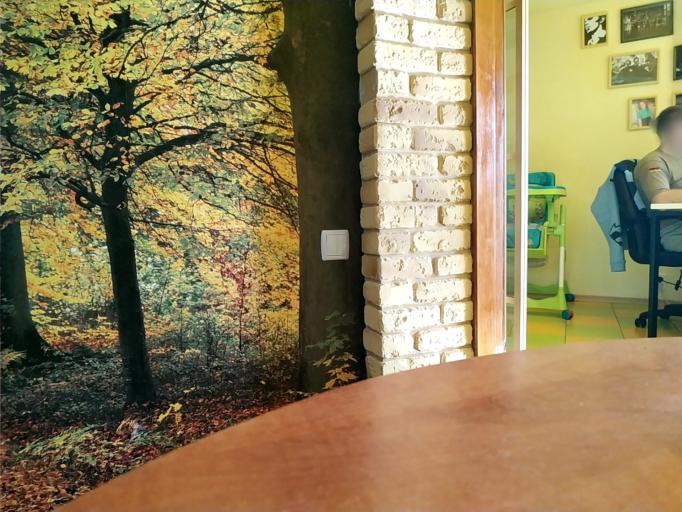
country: RU
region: Tverskaya
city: Vasil'yevskiy Mokh
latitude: 57.1844
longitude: 35.7726
